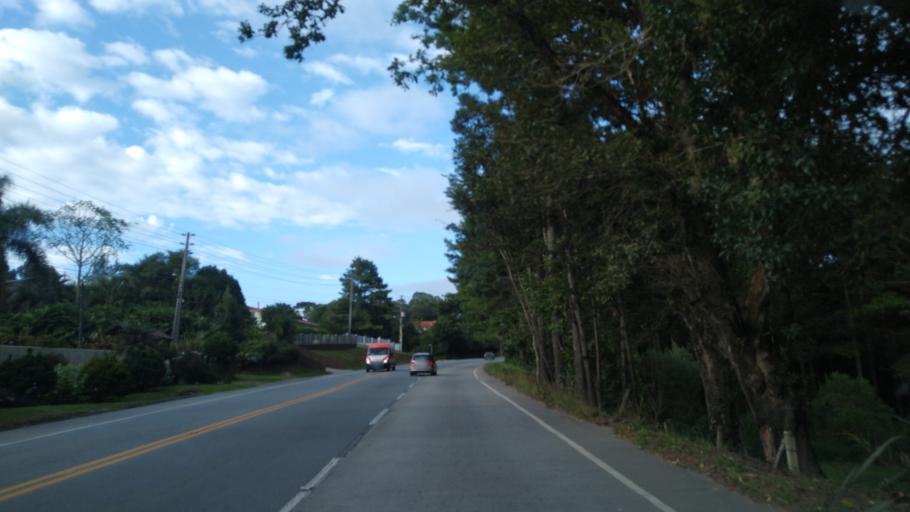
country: BR
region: Santa Catarina
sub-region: Sao Bento Do Sul
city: Sao Bento do Sul
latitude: -26.2423
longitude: -49.4379
